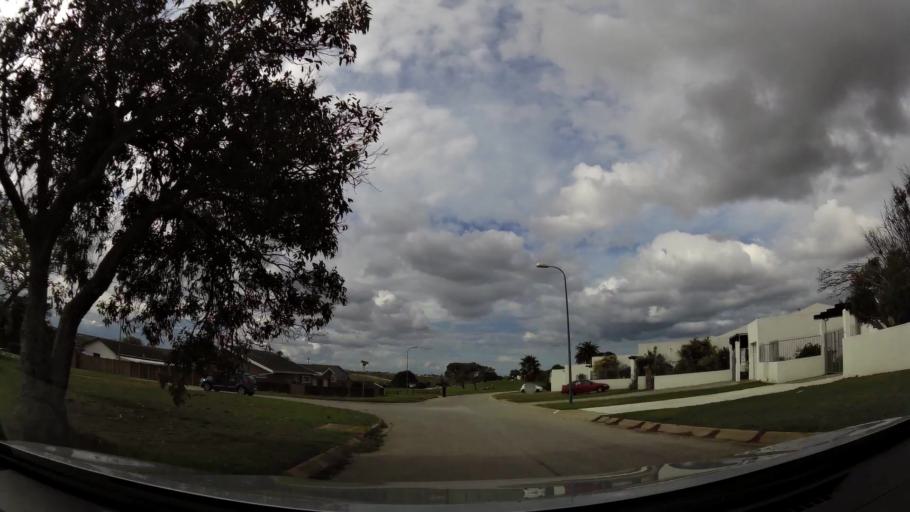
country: ZA
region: Eastern Cape
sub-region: Nelson Mandela Bay Metropolitan Municipality
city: Port Elizabeth
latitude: -33.9328
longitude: 25.5084
